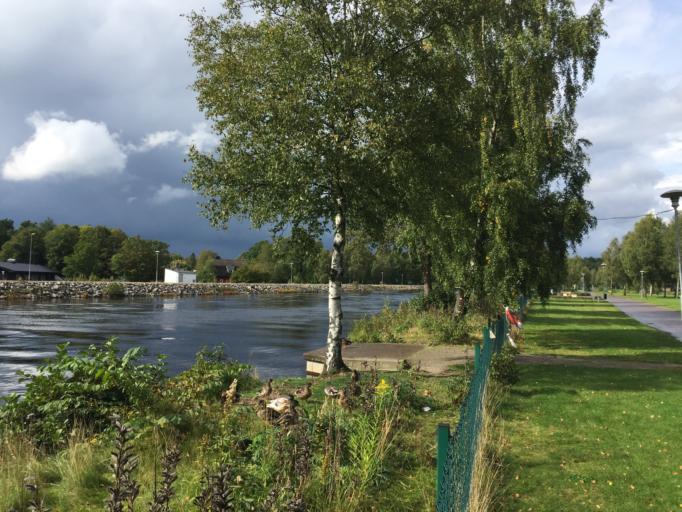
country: SE
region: Kronoberg
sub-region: Markaryds Kommun
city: Stromsnasbruk
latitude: 56.5501
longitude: 13.7291
